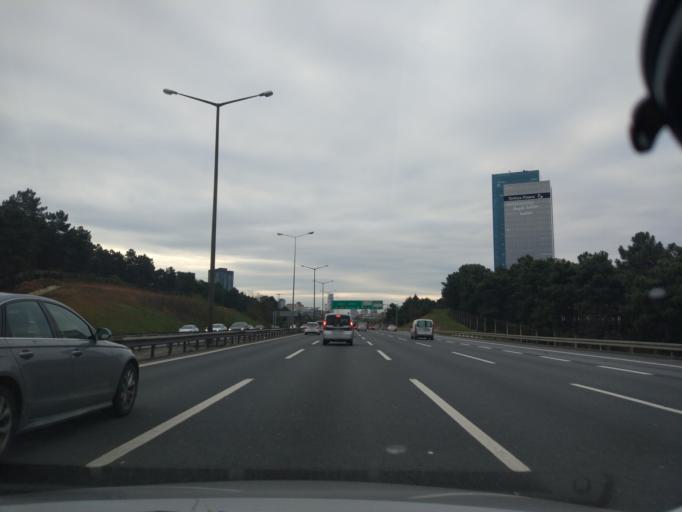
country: TR
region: Istanbul
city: Umraniye
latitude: 41.0398
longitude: 29.1211
